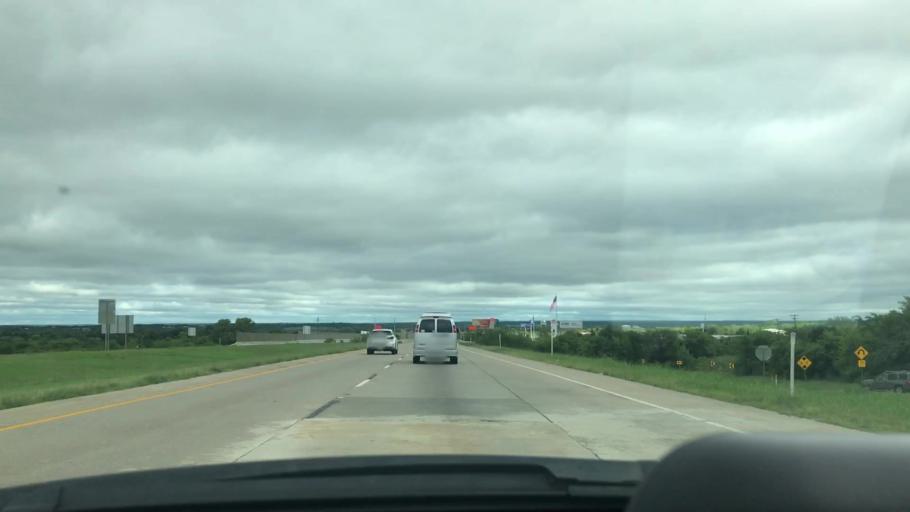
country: US
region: Texas
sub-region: Grayson County
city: Denison
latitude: 33.7682
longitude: -96.5850
